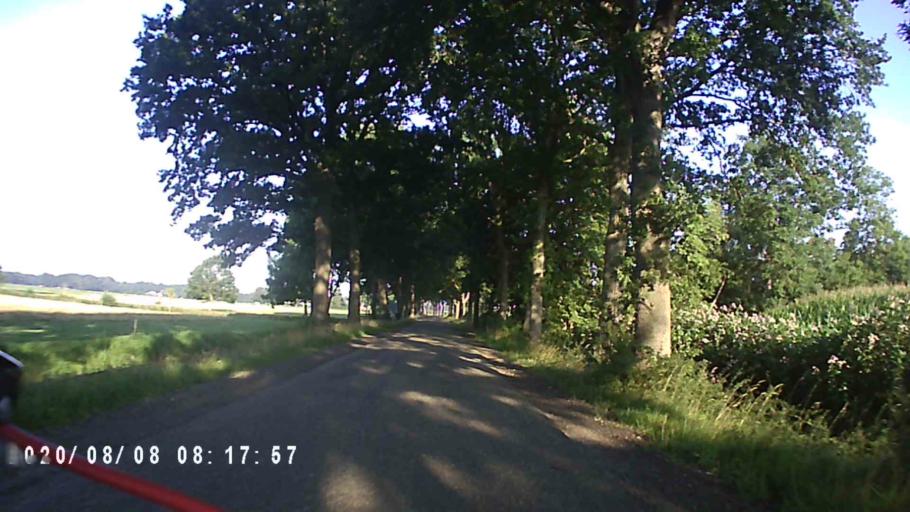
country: NL
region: Groningen
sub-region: Gemeente Leek
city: Leek
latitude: 53.0960
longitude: 6.3265
